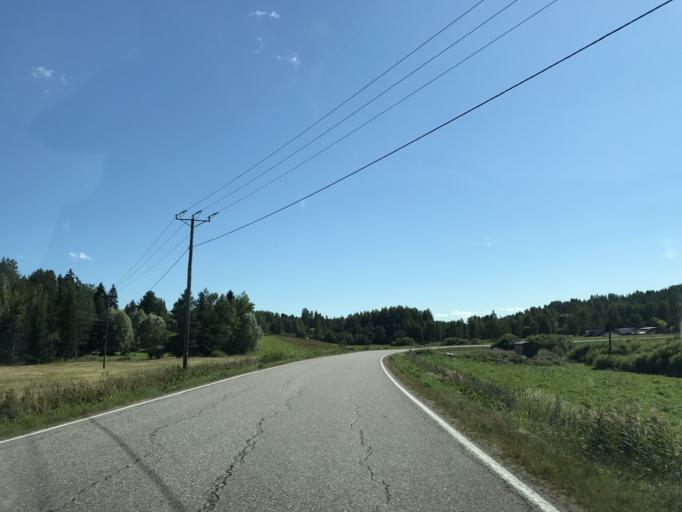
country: FI
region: Paijanne Tavastia
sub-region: Lahti
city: Orimattila
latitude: 60.8042
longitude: 25.6918
